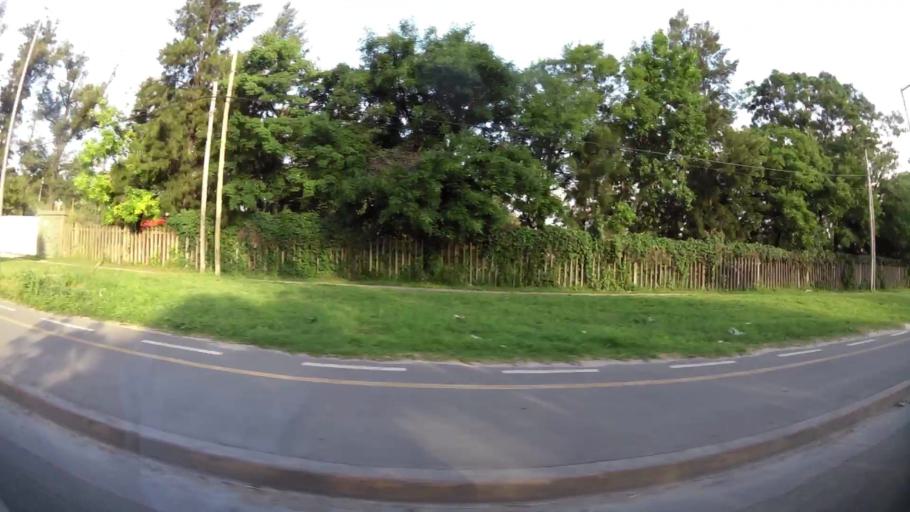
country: AR
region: Buenos Aires
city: Caseros
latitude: -34.5495
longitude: -58.5830
